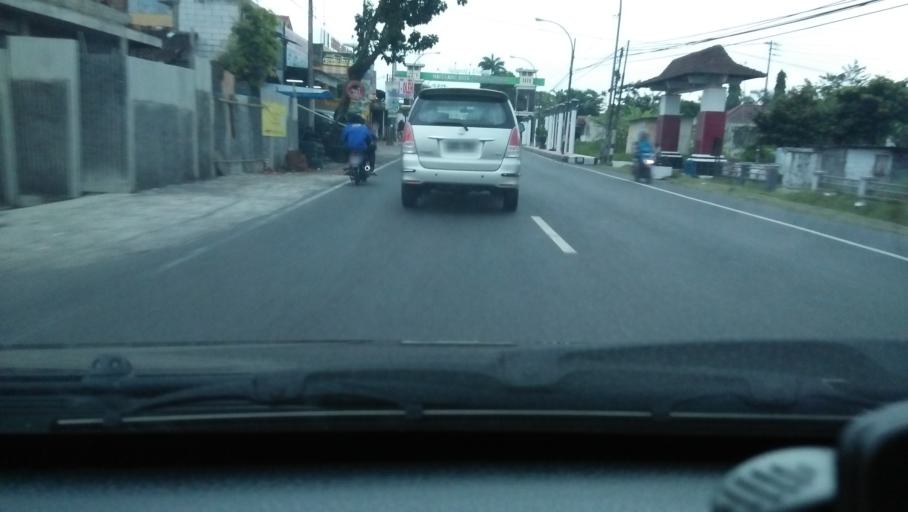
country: ID
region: Central Java
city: Magelang
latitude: -7.4336
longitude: 110.2284
